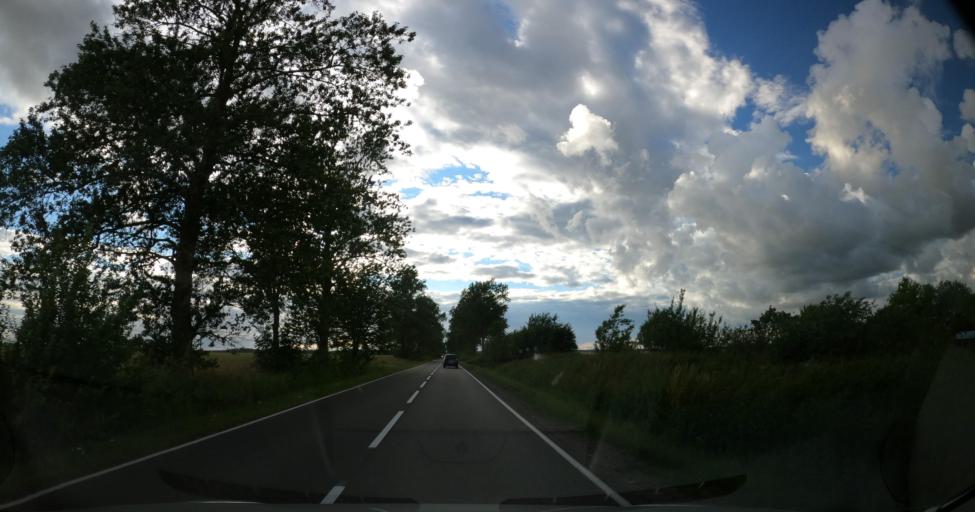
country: PL
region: Pomeranian Voivodeship
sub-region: Powiat slupski
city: Potegowo
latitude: 54.4238
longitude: 17.3766
